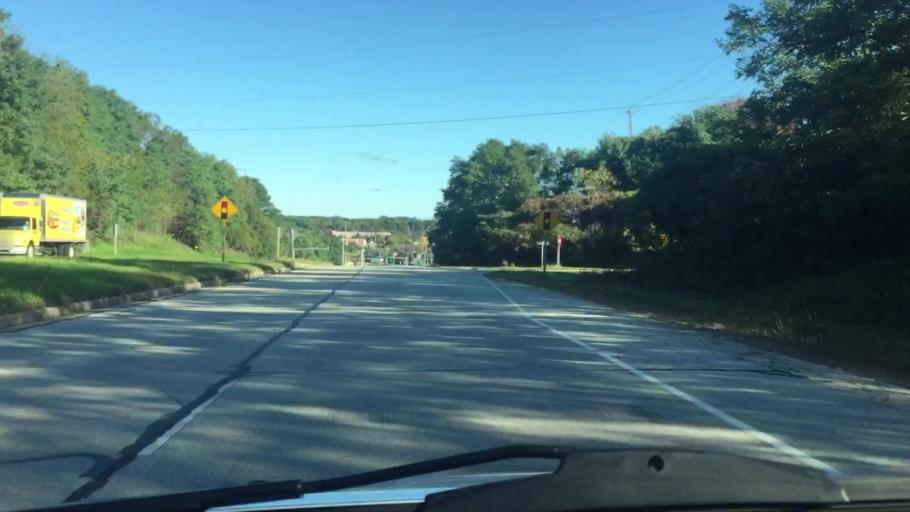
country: US
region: Wisconsin
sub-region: Waukesha County
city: Delafield
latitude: 43.0452
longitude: -88.3739
